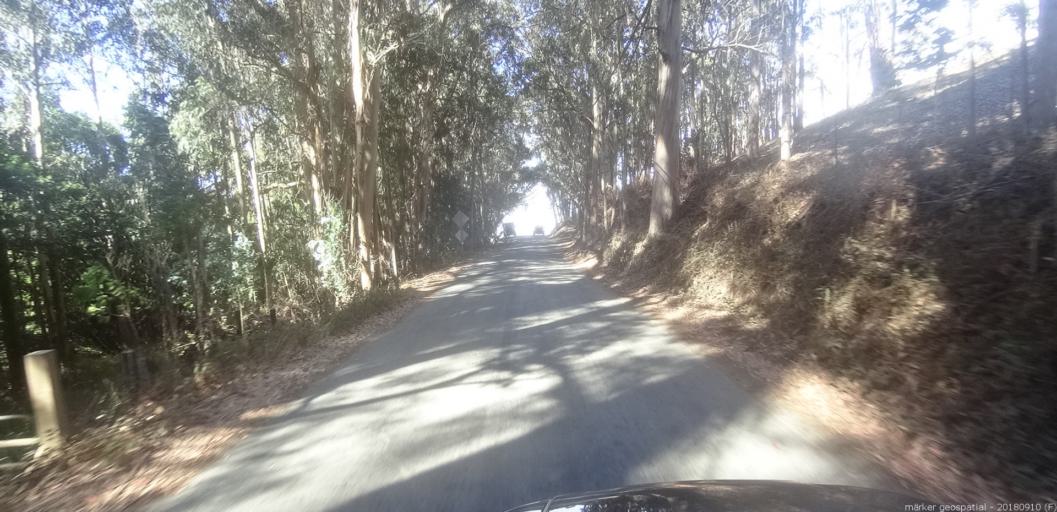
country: US
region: California
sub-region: Monterey County
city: Carmel-by-the-Sea
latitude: 36.3996
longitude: -121.9031
